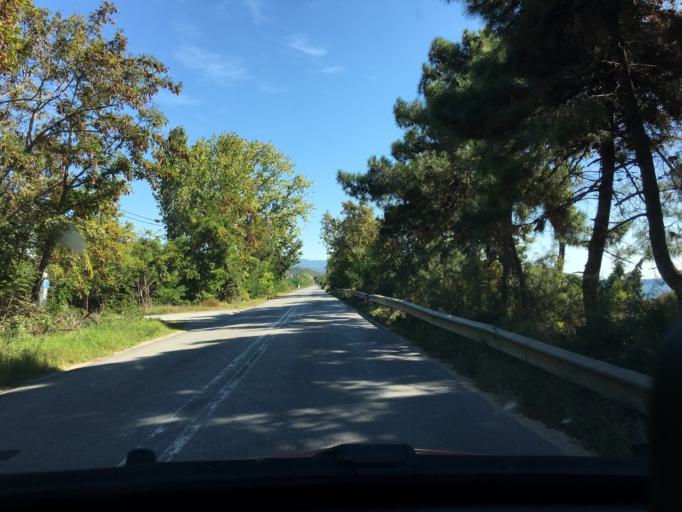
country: GR
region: Central Macedonia
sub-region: Nomos Chalkidikis
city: Nea Roda
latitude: 40.3644
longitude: 23.9215
